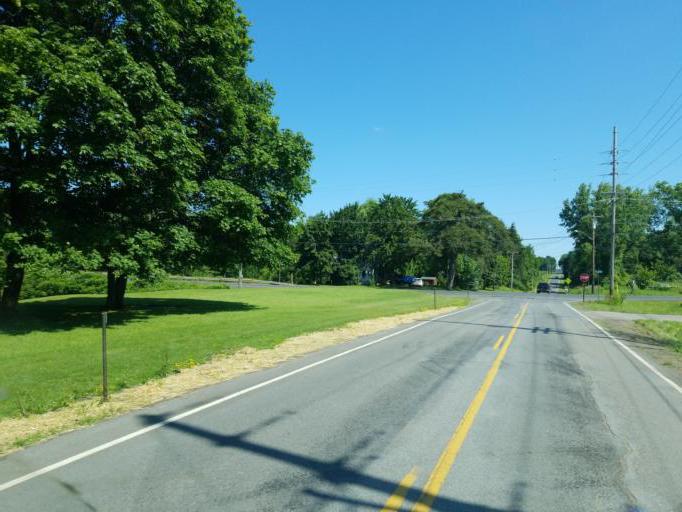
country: US
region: New York
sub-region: Wayne County
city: Wolcott
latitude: 43.2235
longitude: -76.8800
